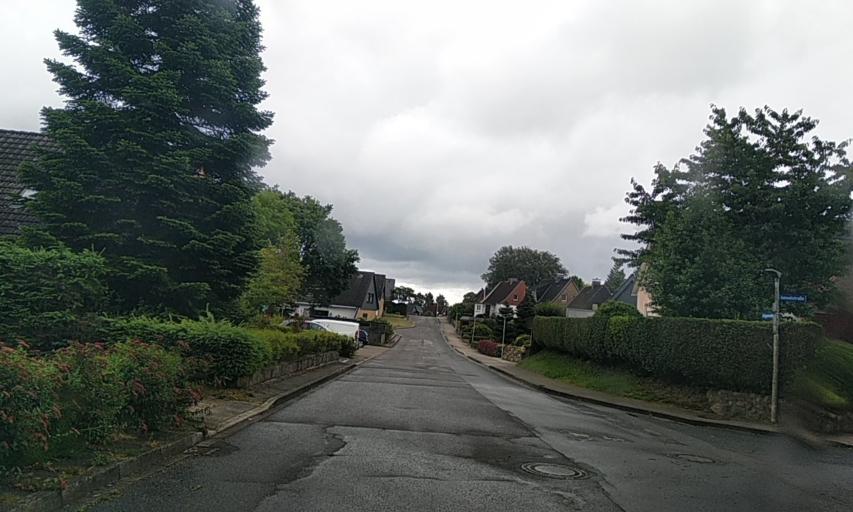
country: DE
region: Schleswig-Holstein
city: Schleswig
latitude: 54.5280
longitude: 9.5467
